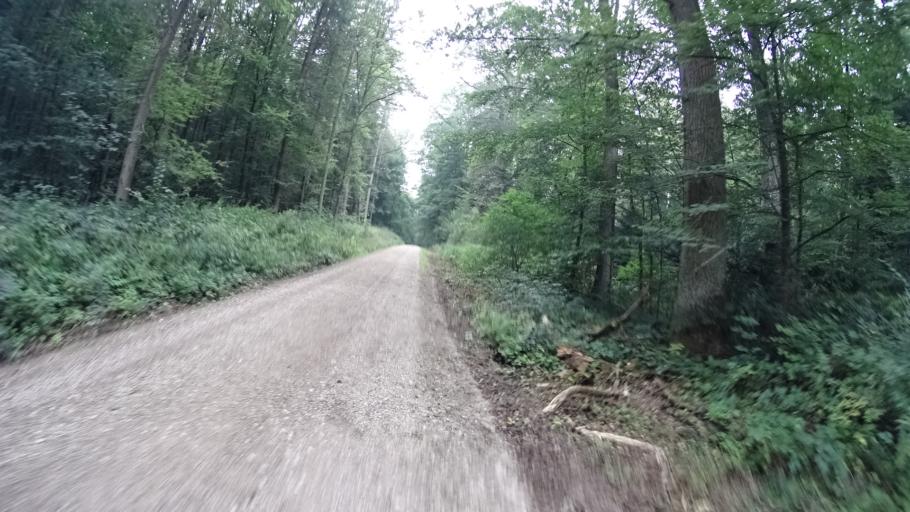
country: DE
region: Bavaria
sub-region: Upper Bavaria
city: Stammham
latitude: 48.8368
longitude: 11.4872
